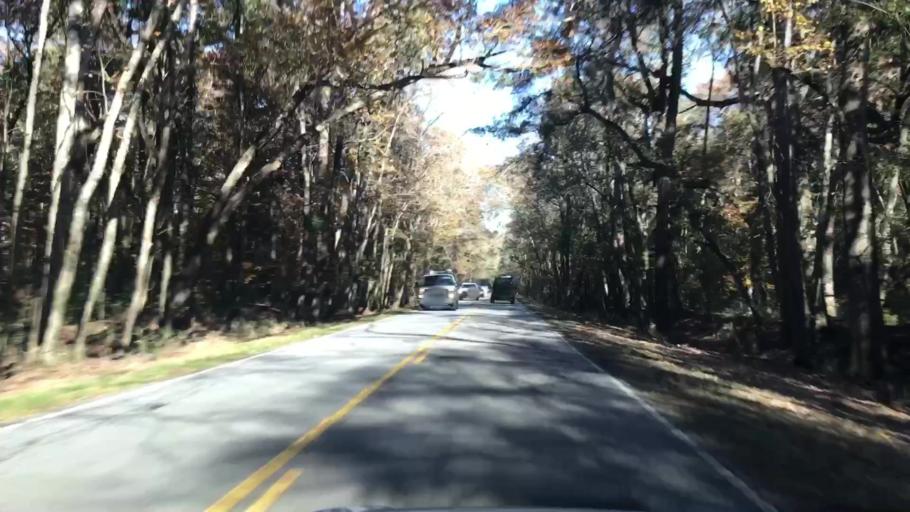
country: US
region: South Carolina
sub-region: Berkeley County
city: Ladson
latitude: 32.9068
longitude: -80.1475
